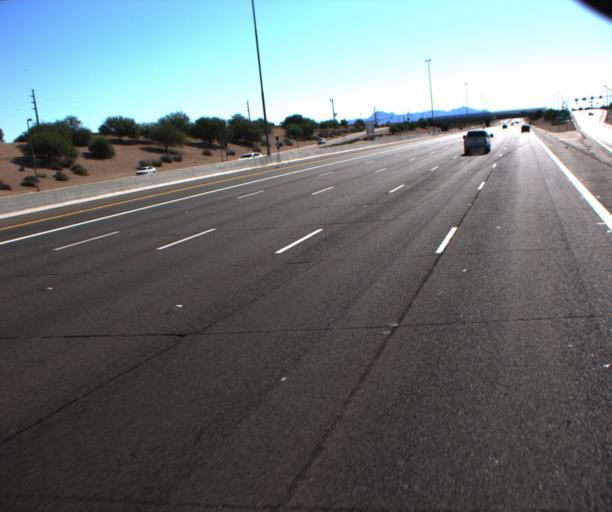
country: US
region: Arizona
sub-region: Maricopa County
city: Gilbert
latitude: 33.3863
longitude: -111.7243
